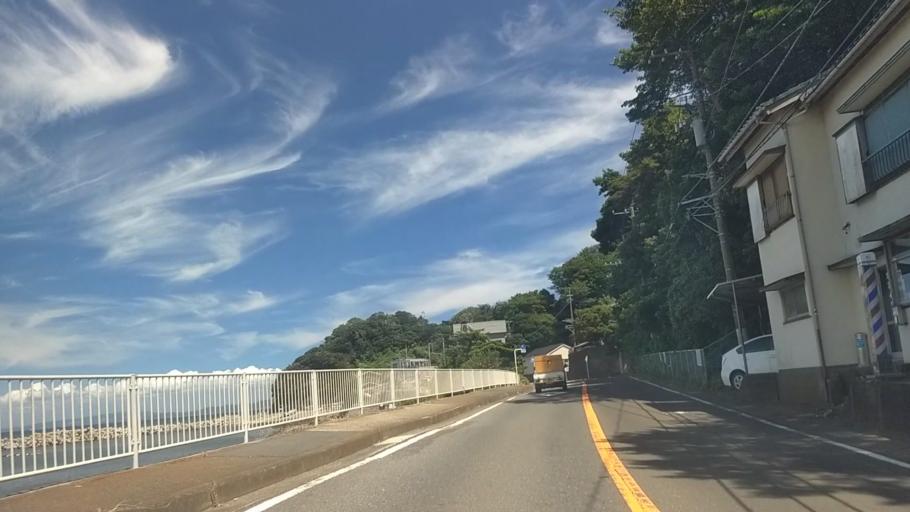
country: JP
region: Kanagawa
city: Miura
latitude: 35.1576
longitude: 139.6678
